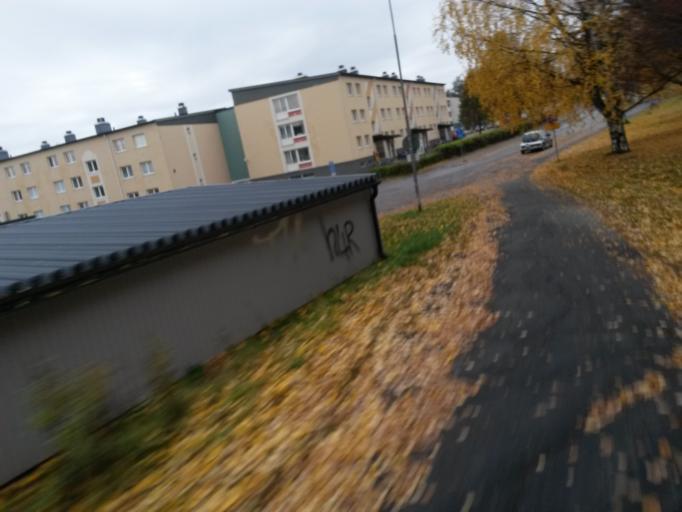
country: SE
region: Vaesterbotten
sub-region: Skelleftea Kommun
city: Skelleftea
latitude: 64.7596
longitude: 20.9740
